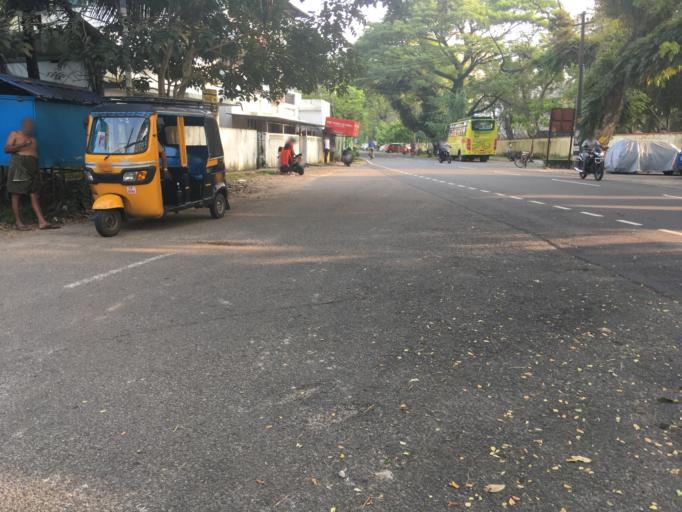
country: IN
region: Kerala
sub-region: Ernakulam
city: Cochin
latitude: 9.9553
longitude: 76.2407
